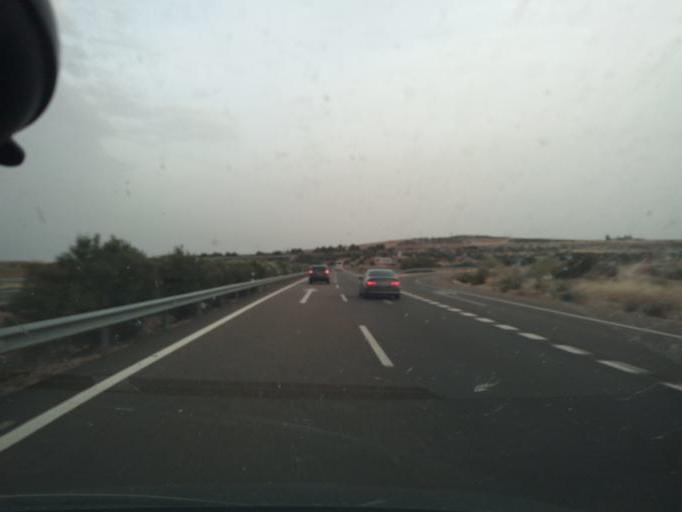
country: ES
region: Extremadura
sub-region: Provincia de Badajoz
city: Merida
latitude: 38.9458
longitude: -6.3318
